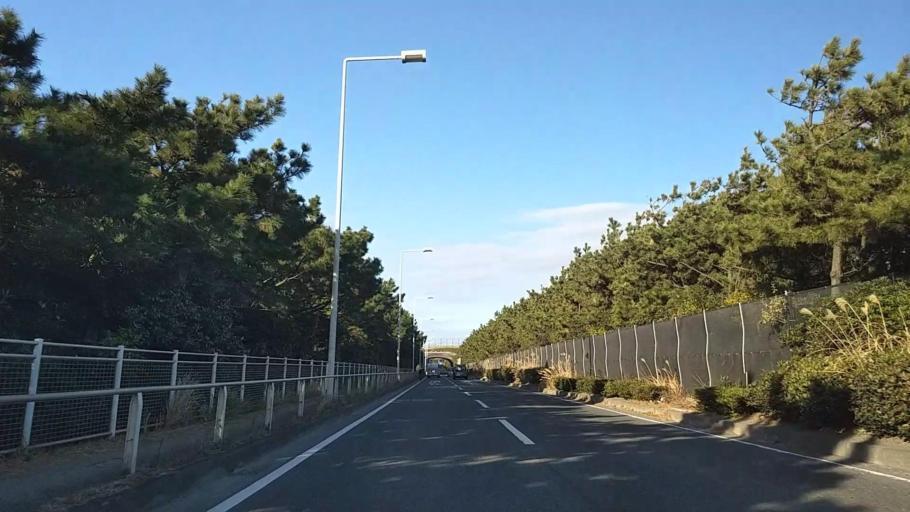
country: JP
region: Kanagawa
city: Fujisawa
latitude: 35.3195
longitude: 139.4497
